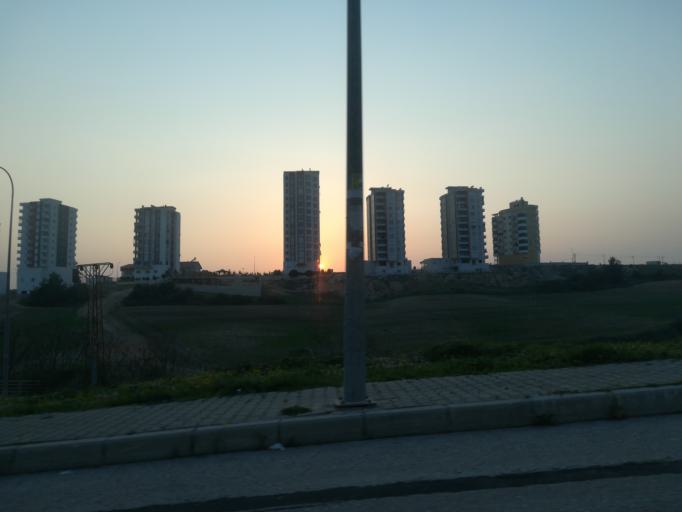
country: TR
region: Adana
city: Adana
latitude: 37.0789
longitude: 35.4127
